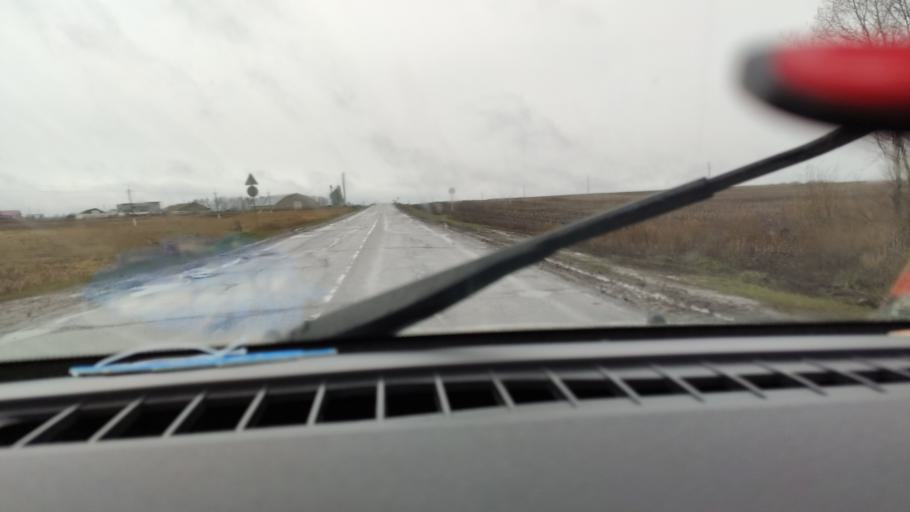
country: RU
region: Tatarstan
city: Nurlat
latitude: 54.6028
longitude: 50.8877
